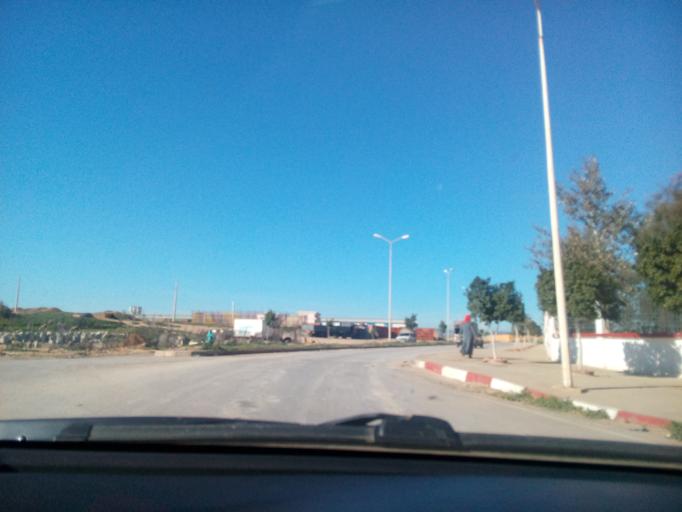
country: DZ
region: Relizane
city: Relizane
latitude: 35.7197
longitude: 0.5290
